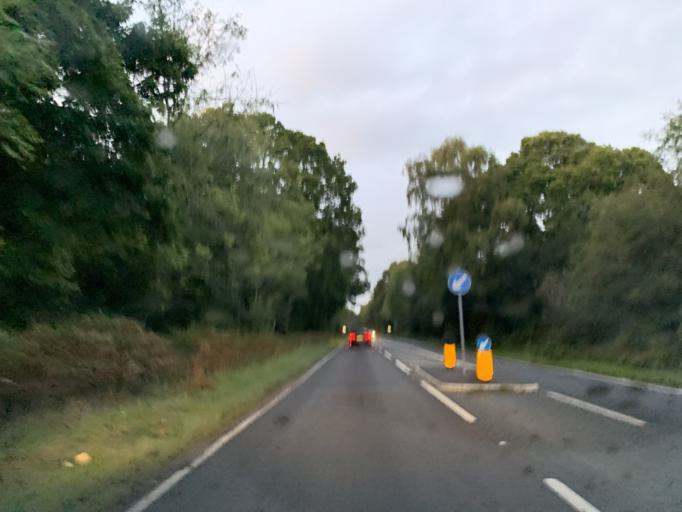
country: GB
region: England
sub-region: Hampshire
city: Brockenhurst
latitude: 50.8293
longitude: -1.5719
